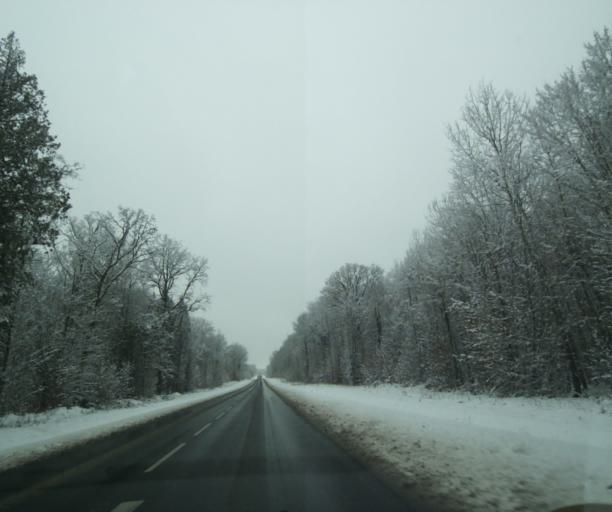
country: FR
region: Champagne-Ardenne
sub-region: Departement de la Haute-Marne
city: Laneuville-a-Remy
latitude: 48.5558
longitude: 4.8387
